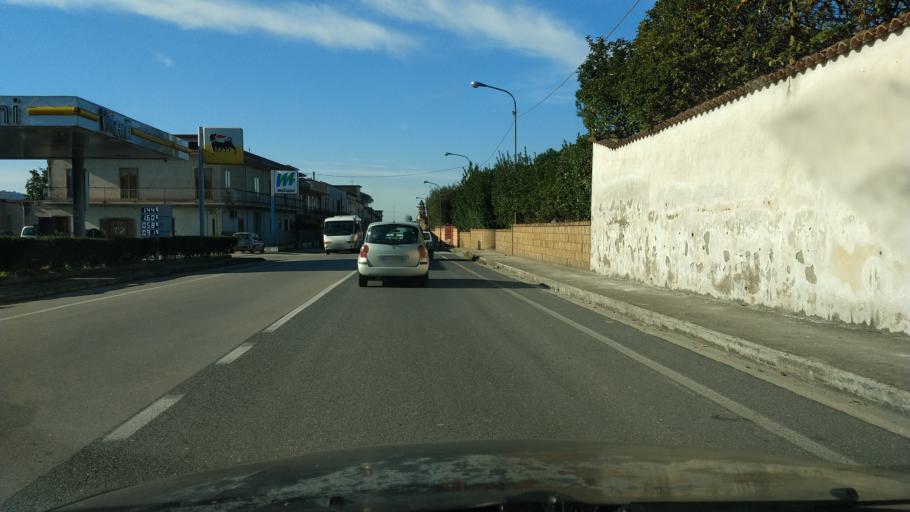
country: IT
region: Campania
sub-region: Provincia di Avellino
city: Avella
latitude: 40.9524
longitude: 14.5936
